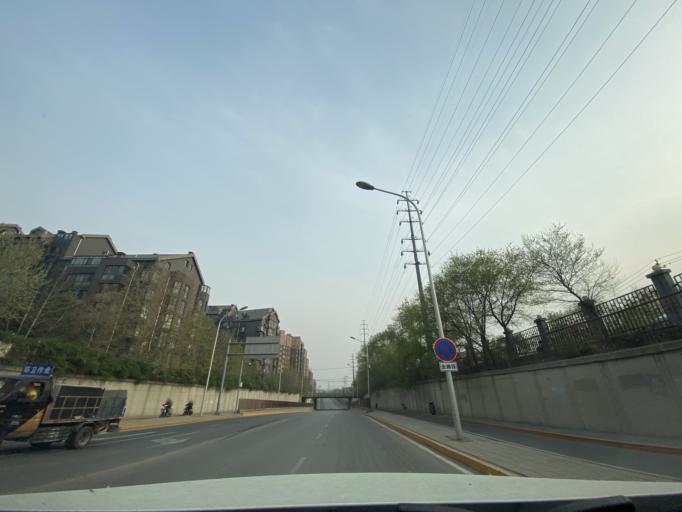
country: CN
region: Beijing
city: Babaoshan
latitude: 39.9323
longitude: 116.2325
